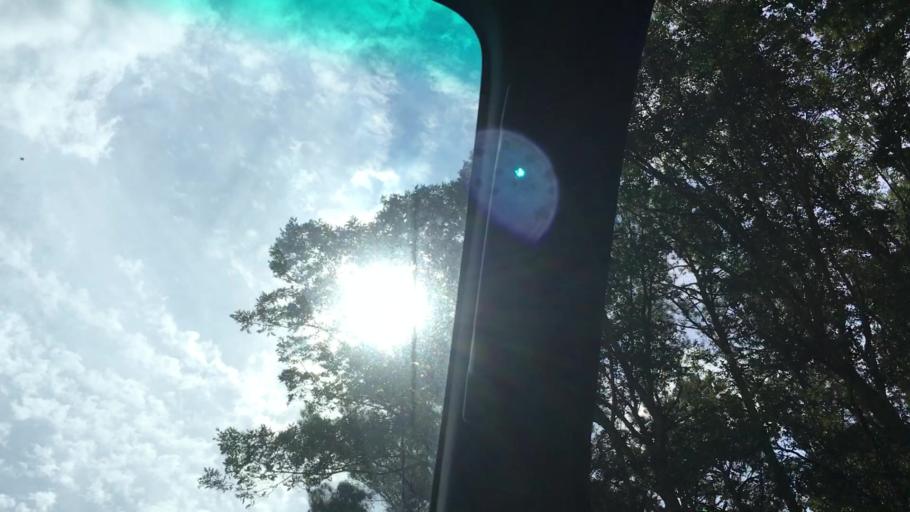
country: US
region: Maryland
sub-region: Worcester County
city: Pocomoke City
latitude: 38.0565
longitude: -75.5572
